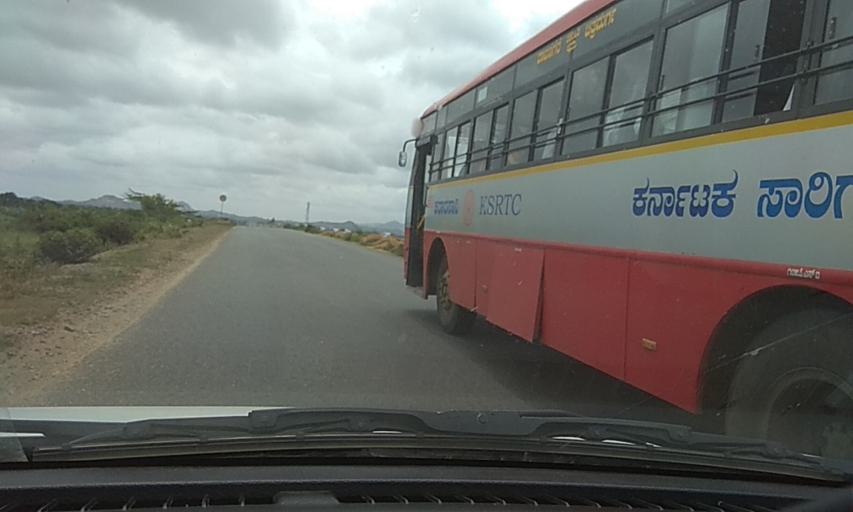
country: IN
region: Karnataka
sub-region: Chitradurga
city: Chitradurga
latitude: 14.2845
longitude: 76.2998
